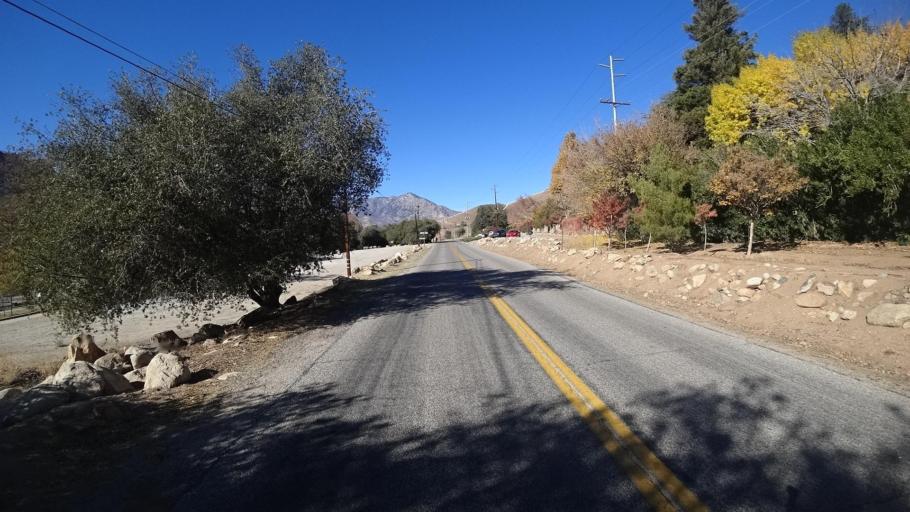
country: US
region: California
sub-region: Kern County
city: Kernville
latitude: 35.7683
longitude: -118.4300
